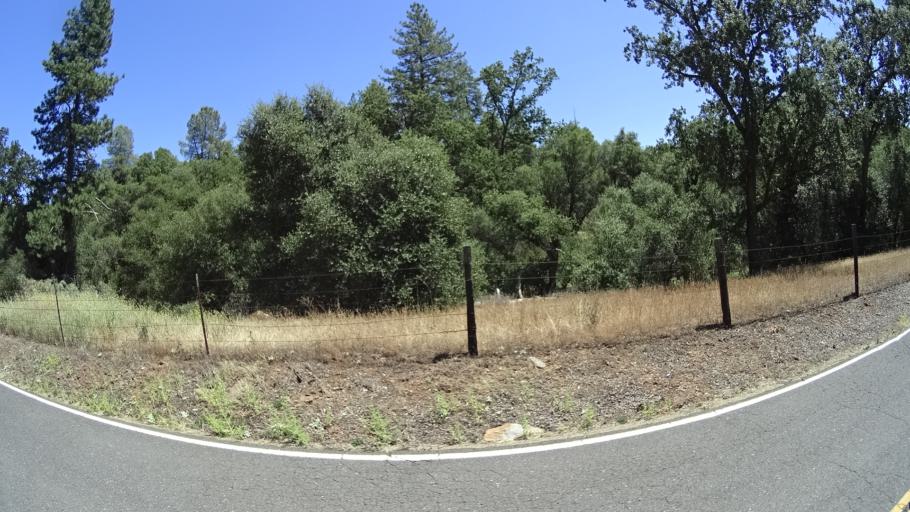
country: US
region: California
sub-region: Calaveras County
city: Murphys
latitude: 38.1254
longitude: -120.5040
